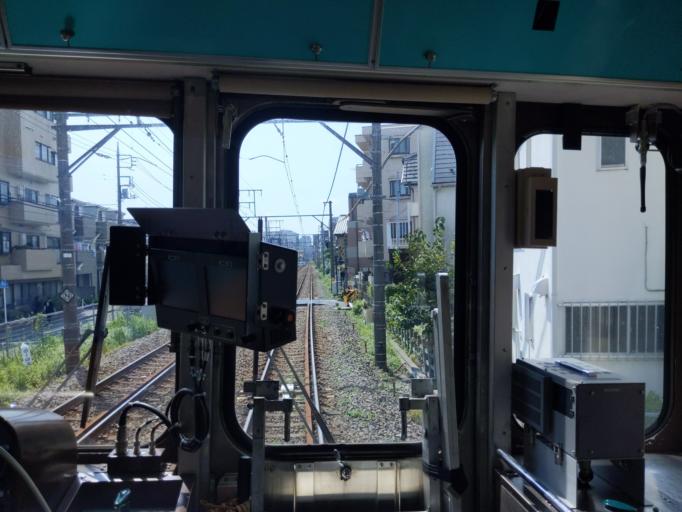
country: JP
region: Kanagawa
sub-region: Kawasaki-shi
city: Kawasaki
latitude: 35.5701
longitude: 139.7059
